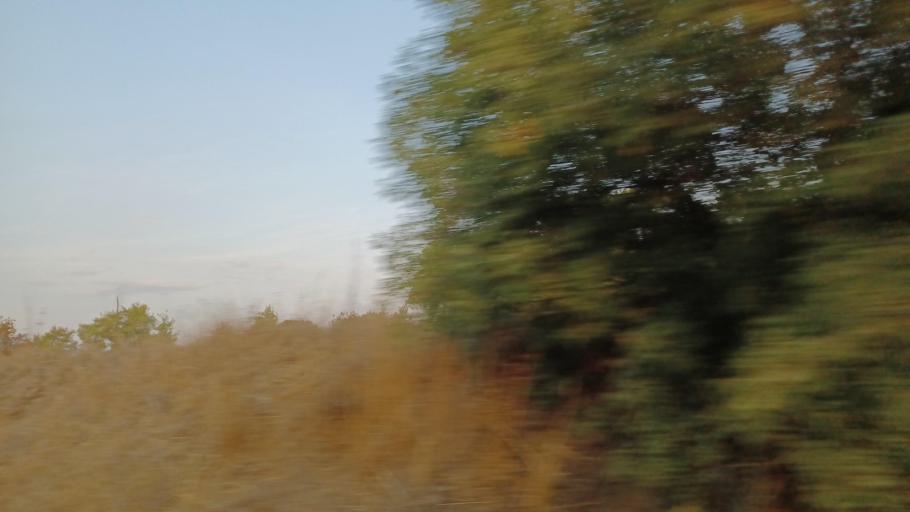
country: CY
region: Larnaka
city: Kornos
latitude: 34.9184
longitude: 33.3846
